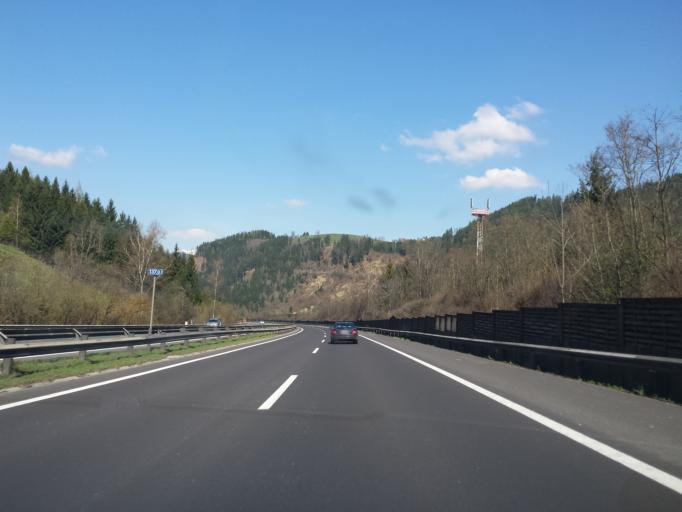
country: AT
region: Styria
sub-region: Politischer Bezirk Leoben
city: Sankt Michael in Obersteiermark
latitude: 47.3134
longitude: 15.0545
